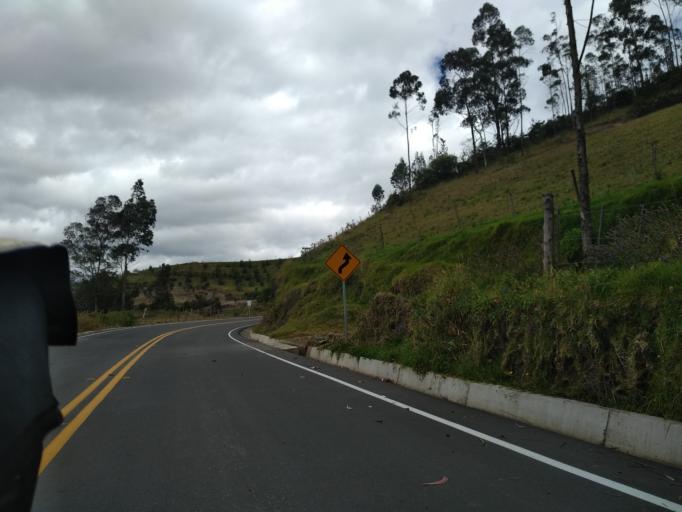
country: EC
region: Cotopaxi
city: Saquisili
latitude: -0.7216
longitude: -78.8905
